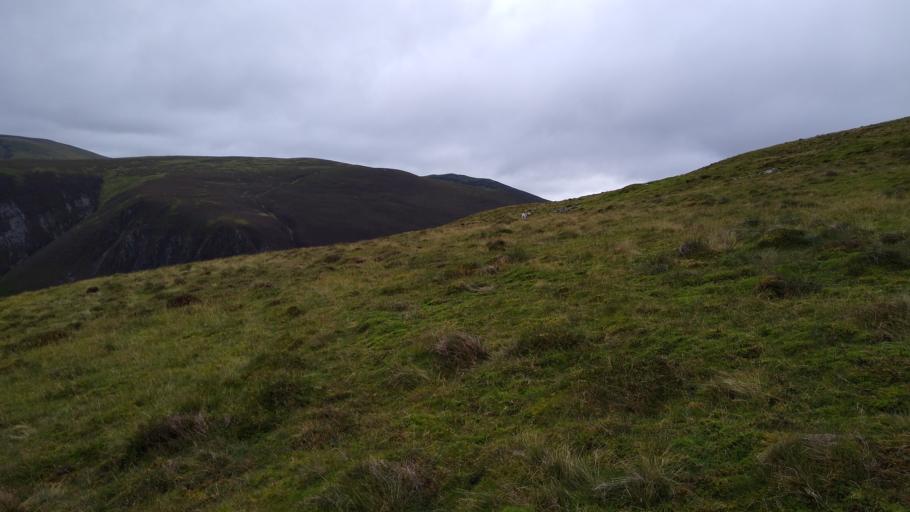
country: GB
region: England
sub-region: Cumbria
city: Keswick
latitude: 54.6711
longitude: -3.1424
